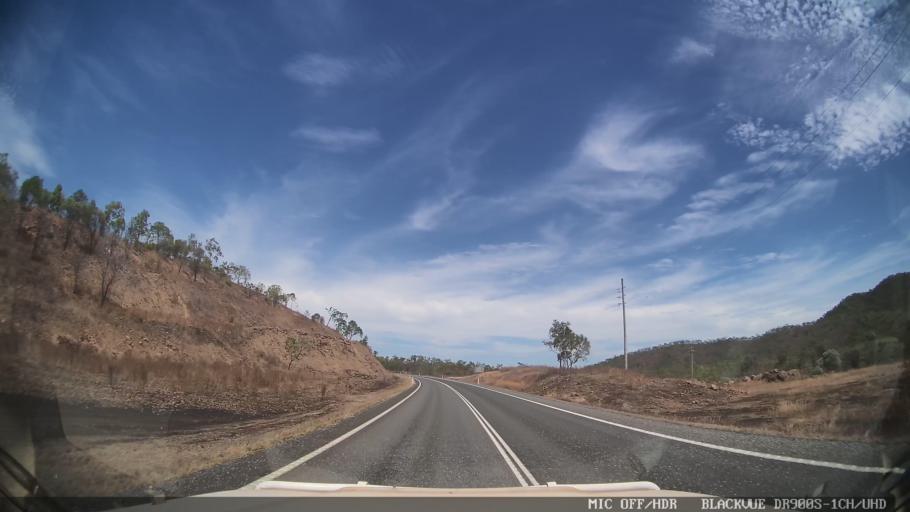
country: AU
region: Queensland
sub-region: Cook
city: Cooktown
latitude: -15.6998
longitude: 145.0270
